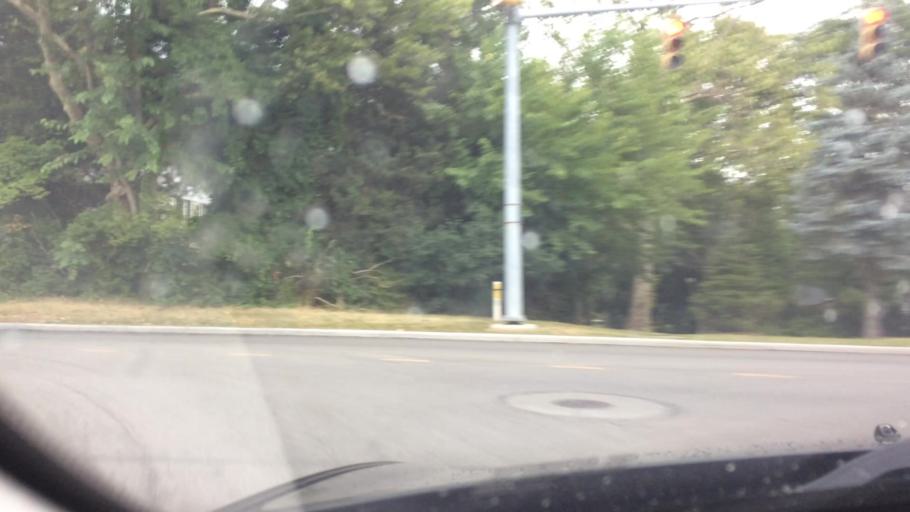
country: US
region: Ohio
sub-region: Lucas County
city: Ottawa Hills
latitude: 41.6625
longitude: -83.6409
